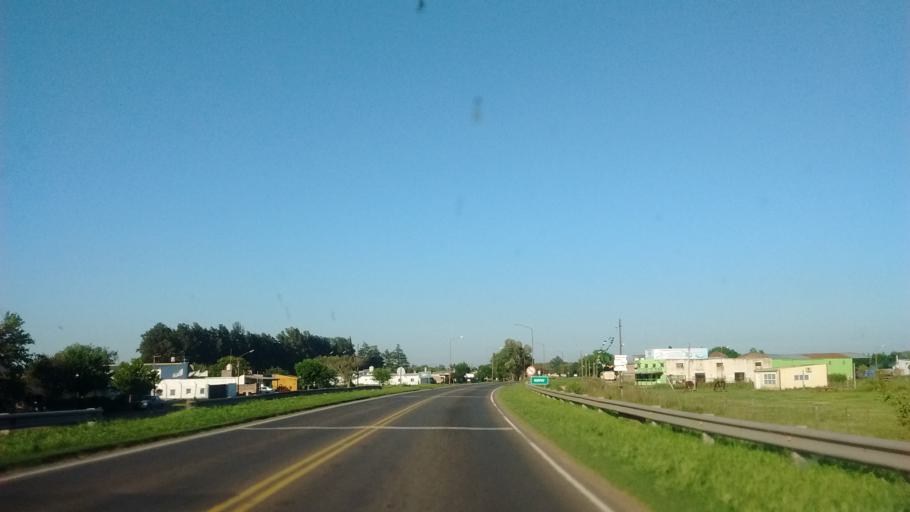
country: AR
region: Santa Fe
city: Venado Tuerto
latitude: -33.6447
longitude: -61.8481
